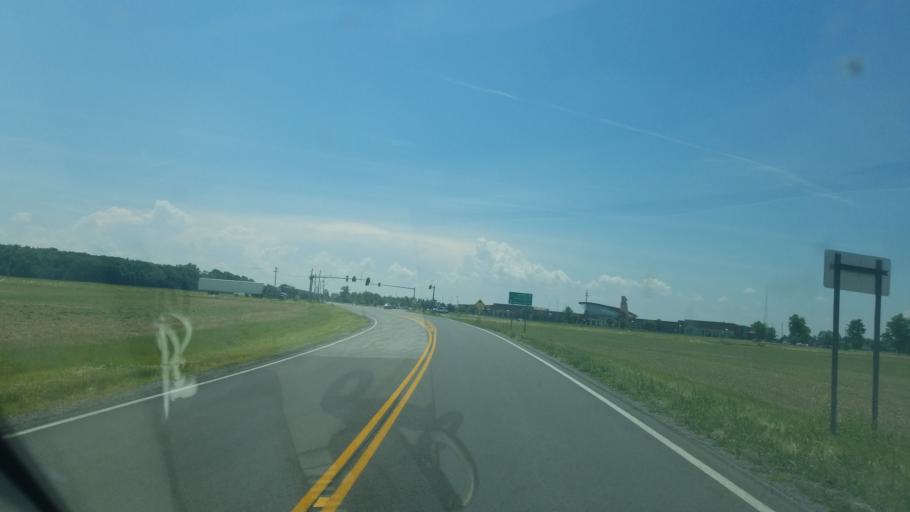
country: US
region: Ohio
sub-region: Hancock County
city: Findlay
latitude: 41.0822
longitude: -83.6181
